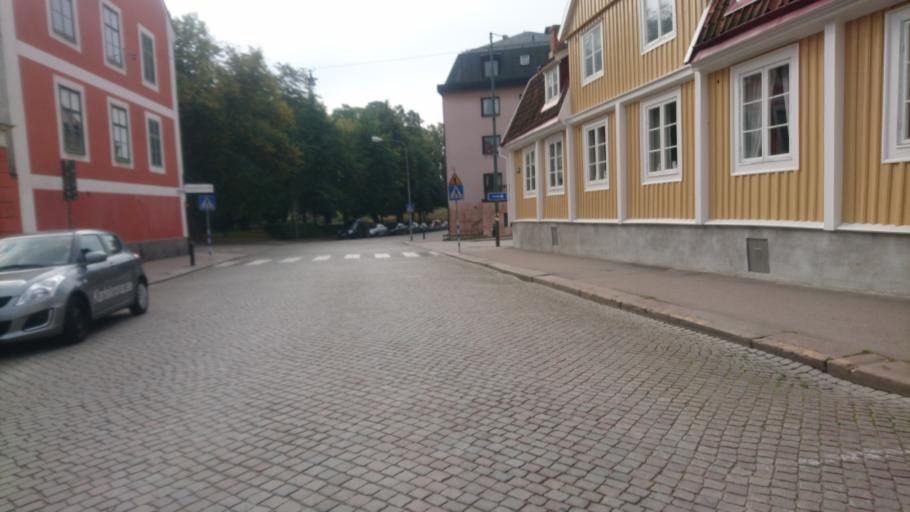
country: SE
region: Blekinge
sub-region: Karlskrona Kommun
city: Karlskrona
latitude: 56.1601
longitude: 15.5852
